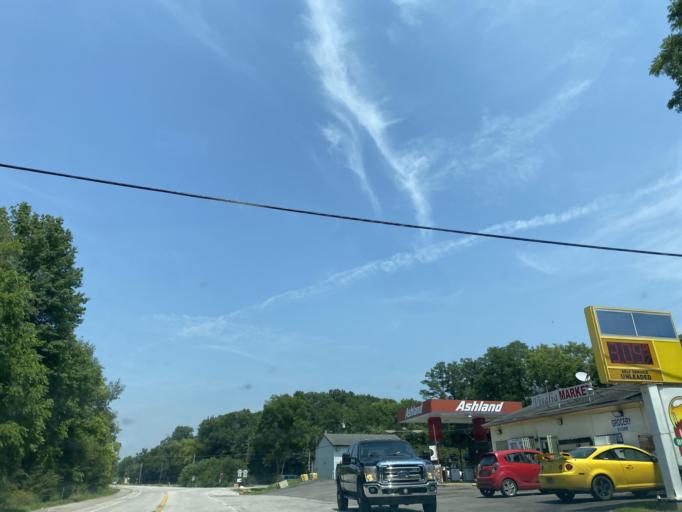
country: US
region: Kentucky
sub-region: Kenton County
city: Ryland Heights
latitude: 38.9186
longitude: -84.4524
